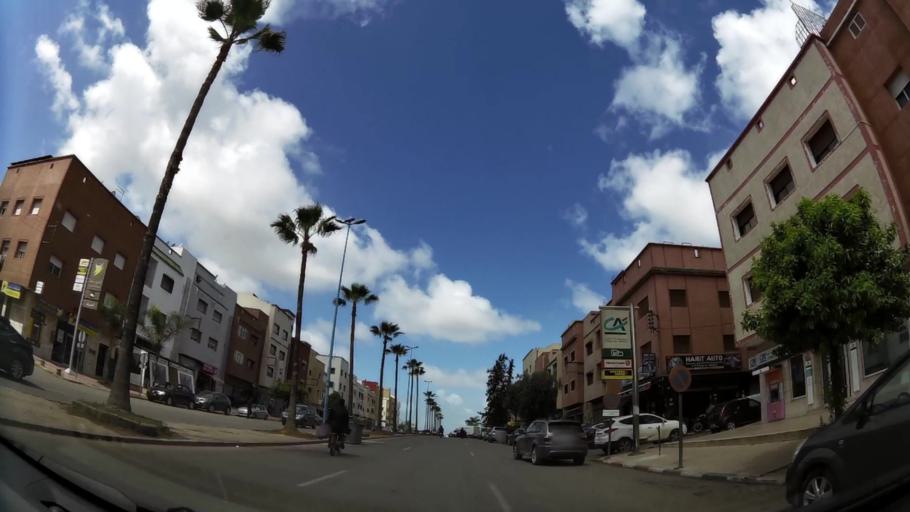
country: MA
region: Grand Casablanca
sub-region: Casablanca
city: Casablanca
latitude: 33.5387
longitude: -7.5918
